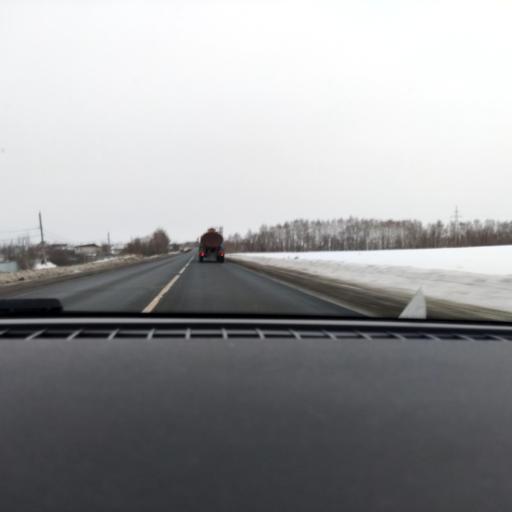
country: RU
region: Samara
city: Smyshlyayevka
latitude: 53.1251
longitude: 50.4199
